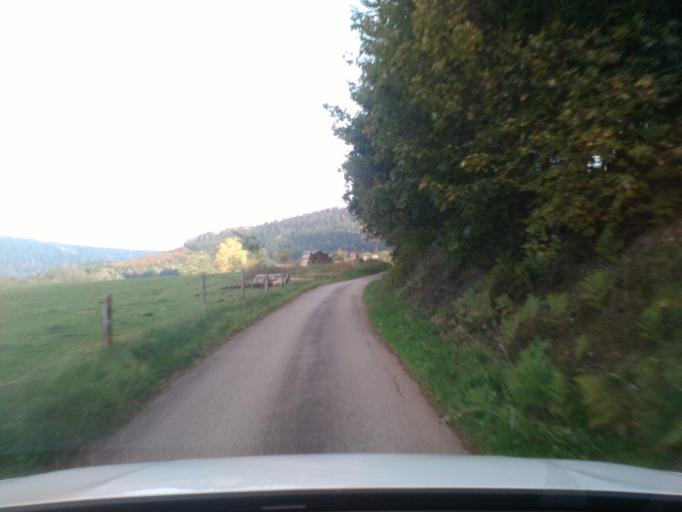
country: FR
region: Lorraine
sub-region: Departement des Vosges
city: Senones
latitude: 48.3992
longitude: 7.0718
